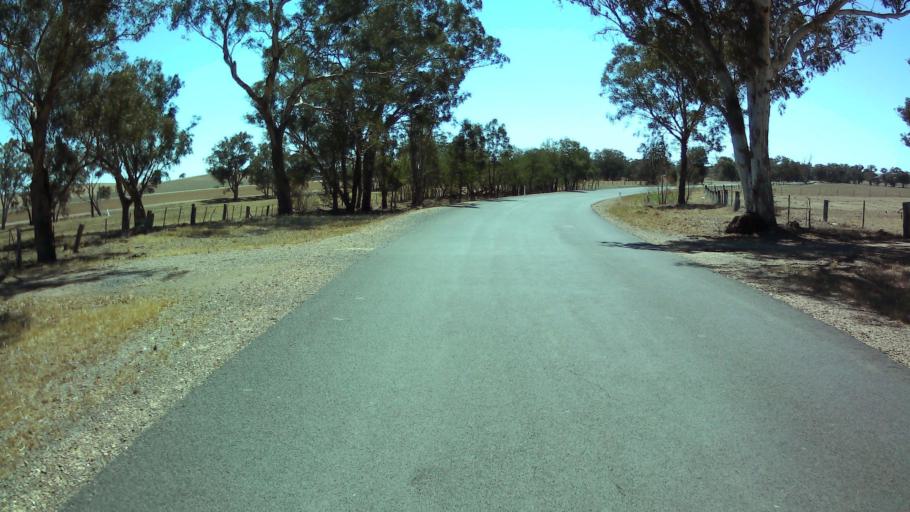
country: AU
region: New South Wales
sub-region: Weddin
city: Grenfell
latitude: -34.0021
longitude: 148.3729
